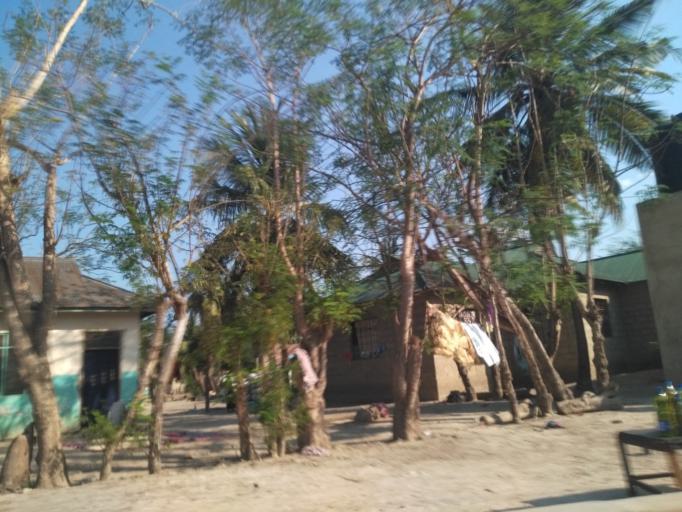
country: TZ
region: Dar es Salaam
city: Dar es Salaam
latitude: -6.8489
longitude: 39.3186
